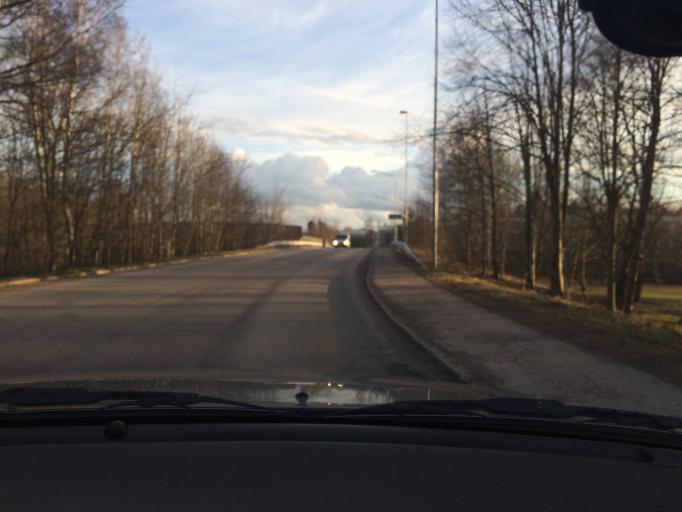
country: SE
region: Vaestmanland
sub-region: Vasteras
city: Vasteras
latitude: 59.6112
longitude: 16.5890
